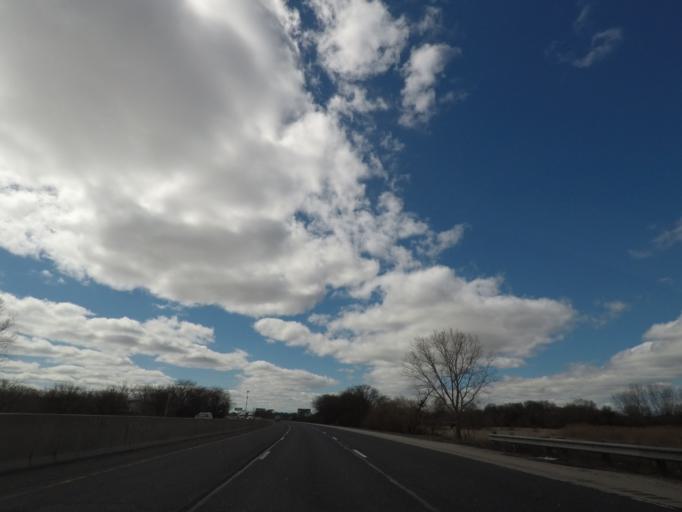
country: US
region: Illinois
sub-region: Will County
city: Plainfield
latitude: 41.6330
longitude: -88.1628
